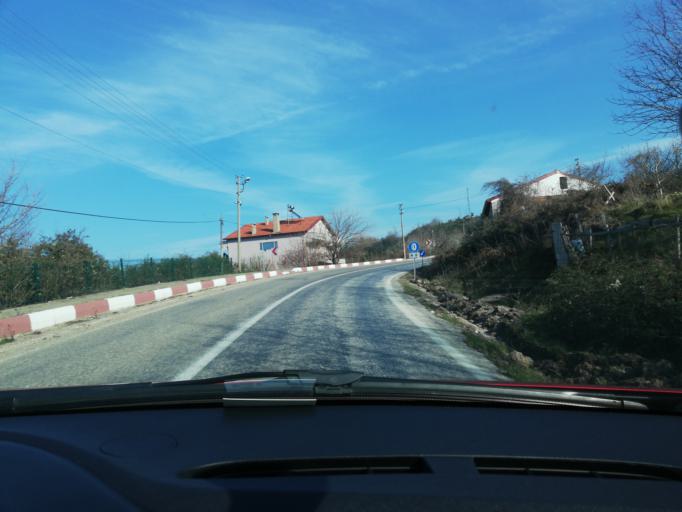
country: TR
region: Bartin
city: Kurucasile
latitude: 41.8476
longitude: 32.7349
